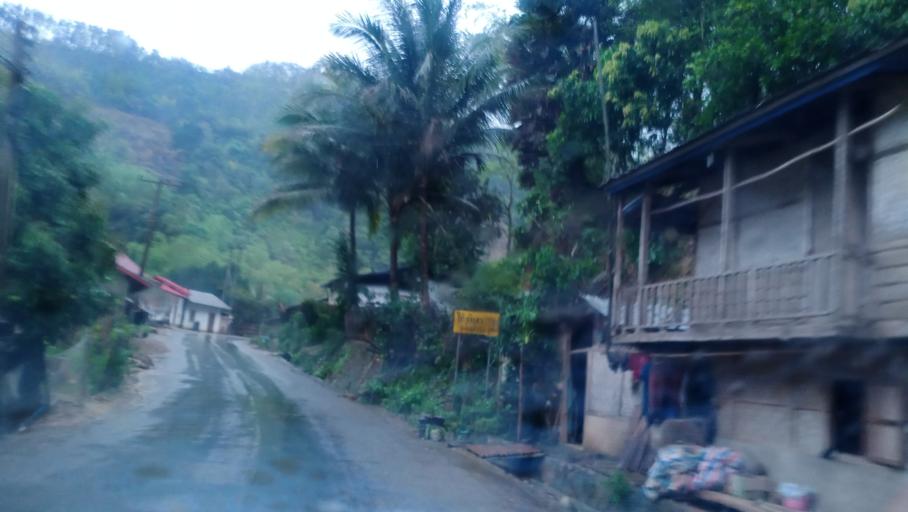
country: LA
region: Phongsali
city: Khoa
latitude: 21.0746
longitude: 102.5028
